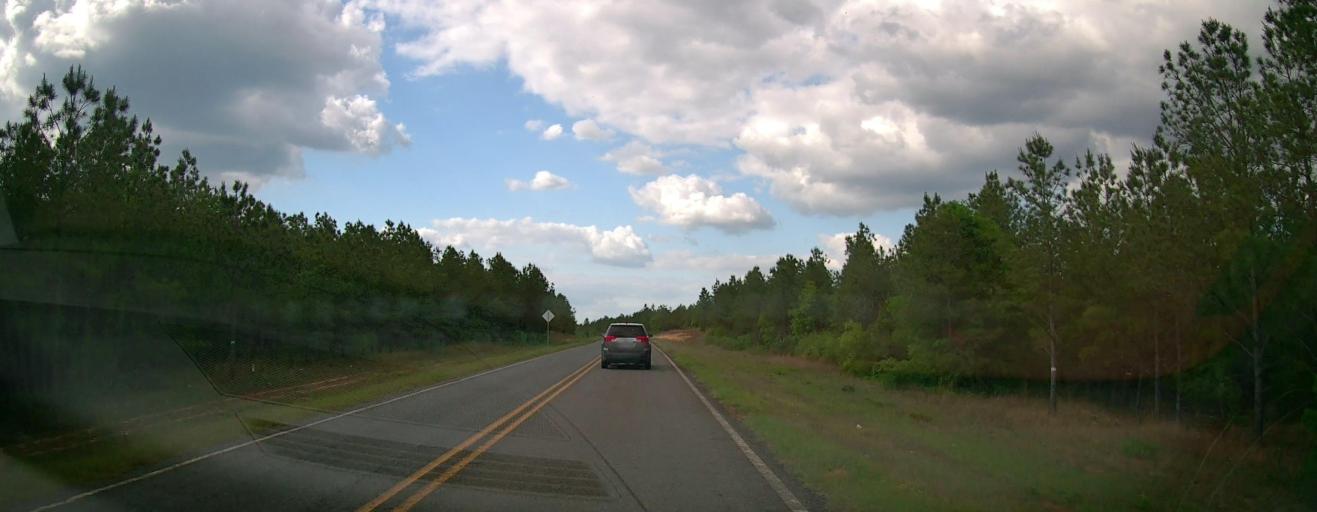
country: US
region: Georgia
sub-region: Johnson County
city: Wrightsville
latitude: 32.7516
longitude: -82.9265
